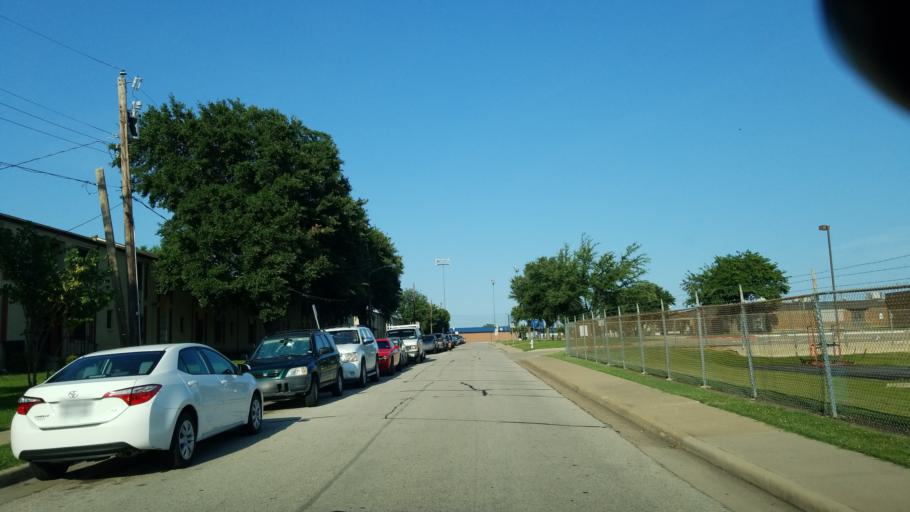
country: US
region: Texas
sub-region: Dallas County
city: Carrollton
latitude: 32.9460
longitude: -96.8953
